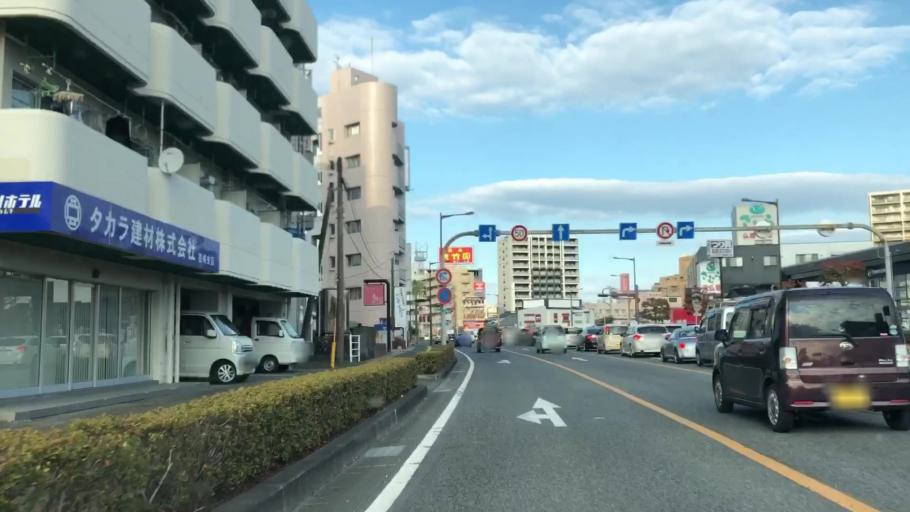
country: JP
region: Miyazaki
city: Miyazaki-shi
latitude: 31.8921
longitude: 131.4152
